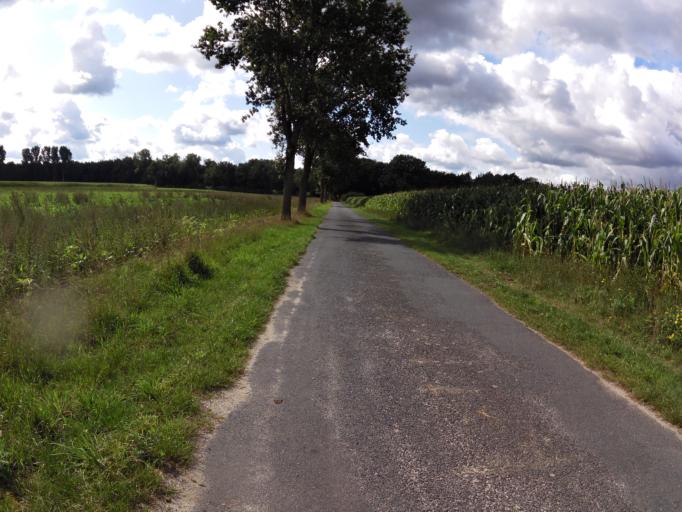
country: DE
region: Lower Saxony
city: Sandbostel
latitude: 53.3833
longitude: 9.1451
